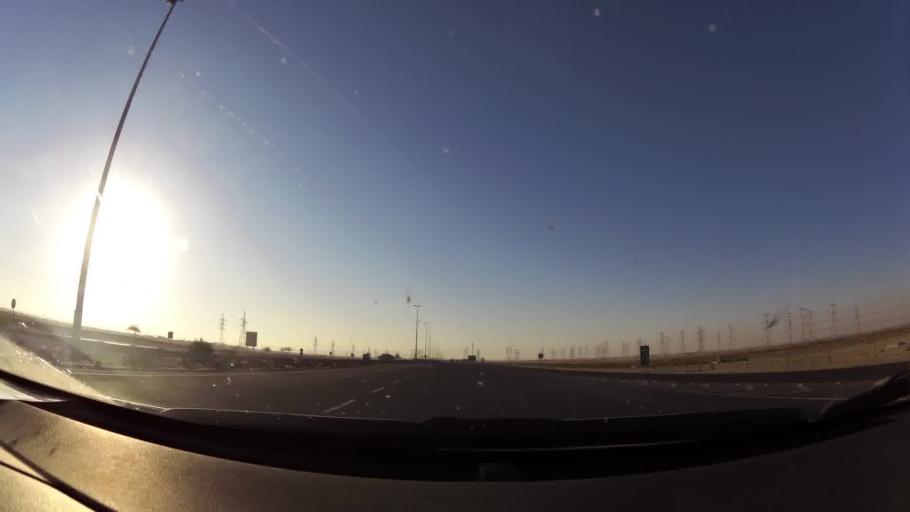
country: KW
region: Al Ahmadi
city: Al Fahahil
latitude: 28.7759
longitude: 48.2763
